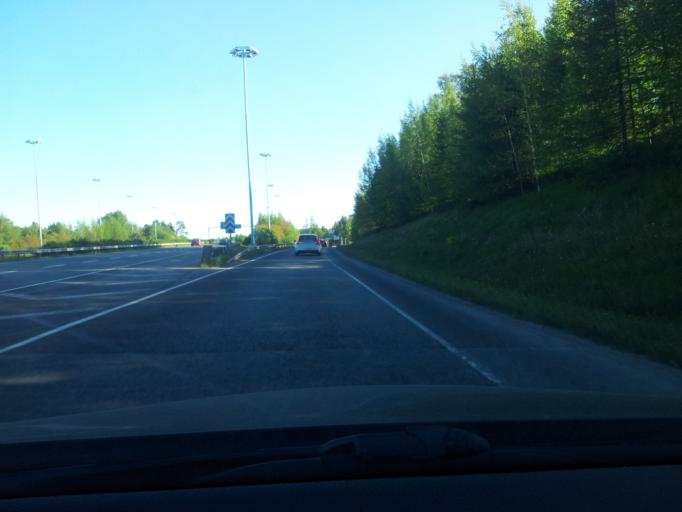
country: FI
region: Uusimaa
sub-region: Helsinki
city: Koukkuniemi
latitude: 60.1727
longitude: 24.7544
